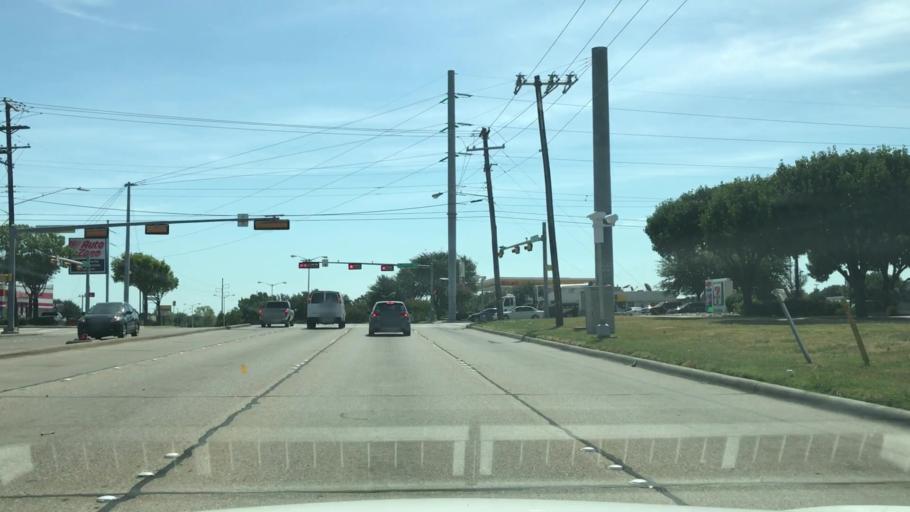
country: US
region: Texas
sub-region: Dallas County
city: Garland
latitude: 32.9446
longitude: -96.6659
